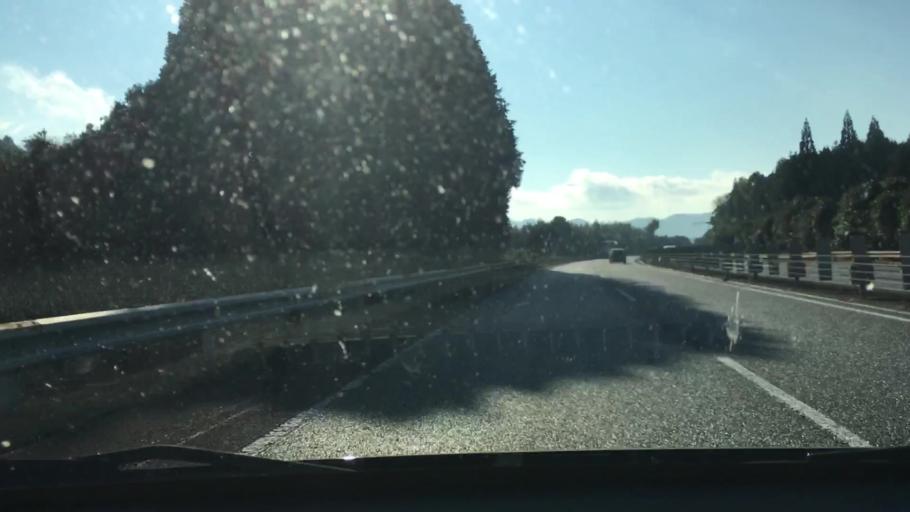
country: JP
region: Kagoshima
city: Okuchi-shinohara
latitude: 32.0178
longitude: 130.7699
